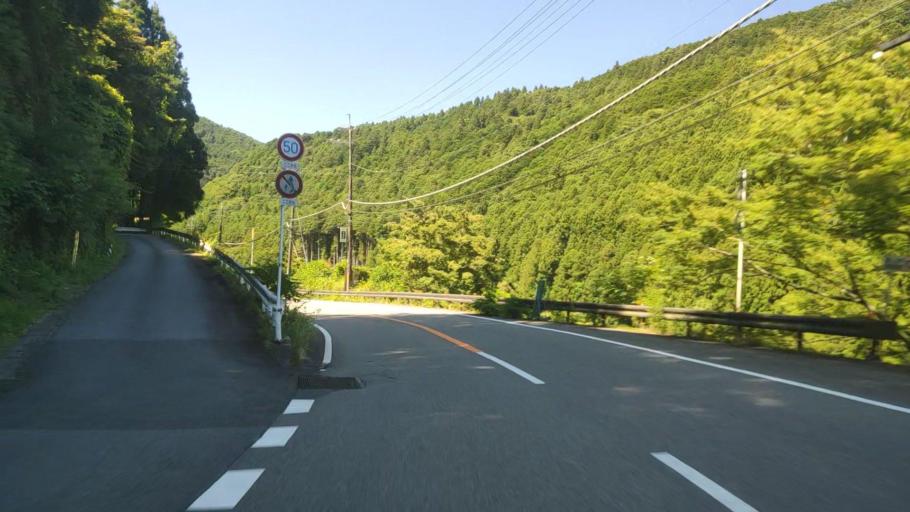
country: JP
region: Nara
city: Yoshino-cho
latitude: 34.2858
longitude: 136.0037
